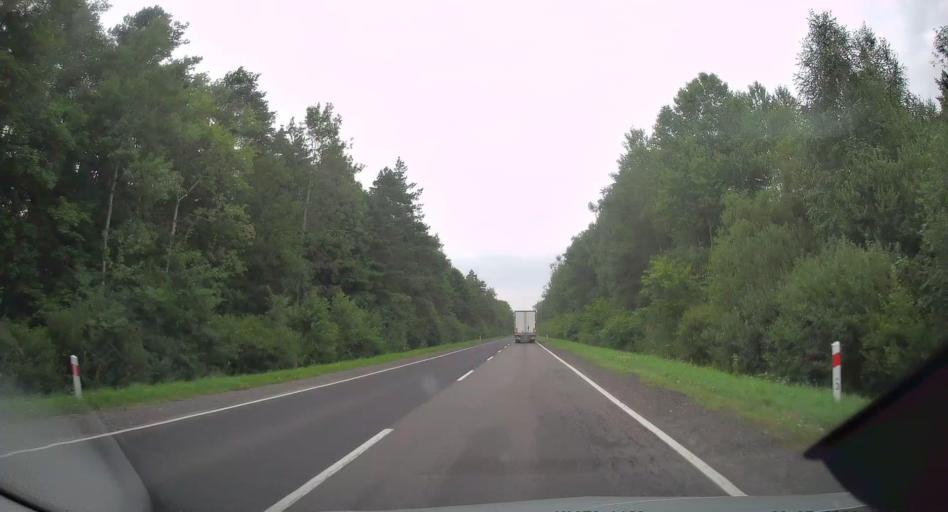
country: PL
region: Lodz Voivodeship
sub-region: Powiat radomszczanski
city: Radomsko
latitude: 51.0363
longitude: 19.4363
